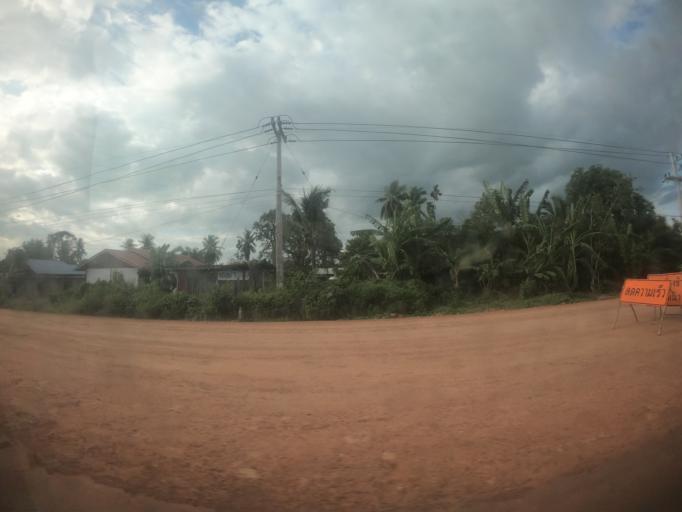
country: TH
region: Surin
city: Kap Choeng
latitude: 14.4703
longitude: 103.6182
